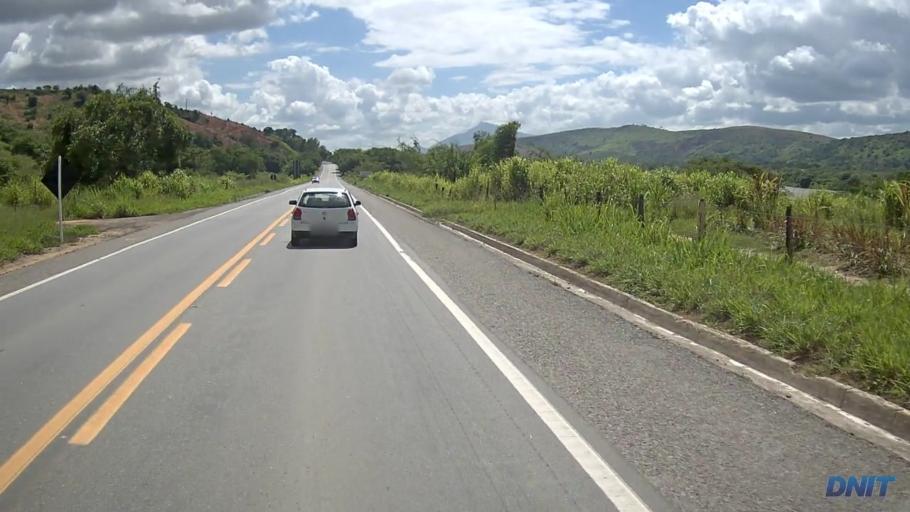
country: BR
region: Minas Gerais
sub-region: Governador Valadares
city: Governador Valadares
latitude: -18.9654
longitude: -42.0813
